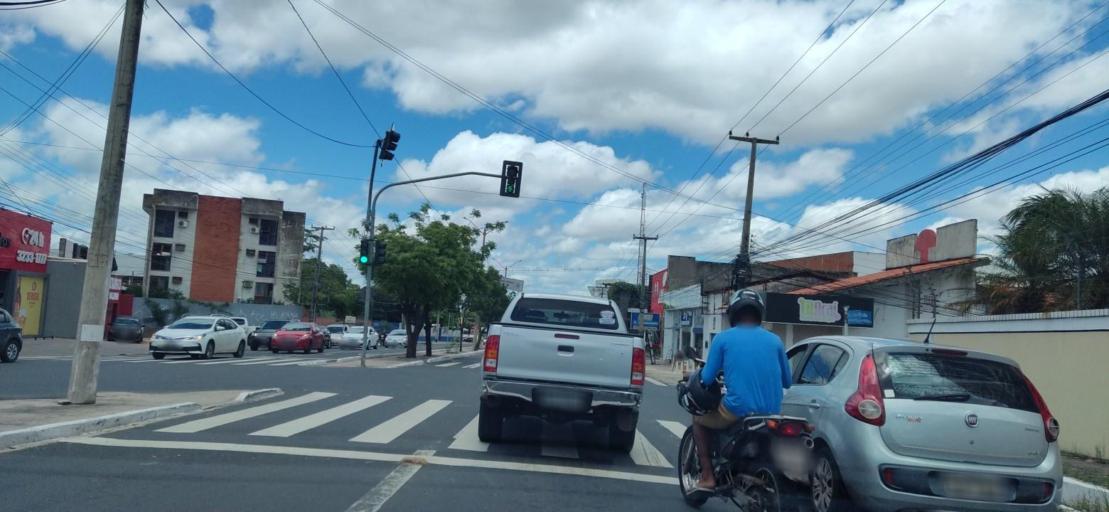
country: BR
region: Piaui
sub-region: Teresina
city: Teresina
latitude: -5.0658
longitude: -42.7703
